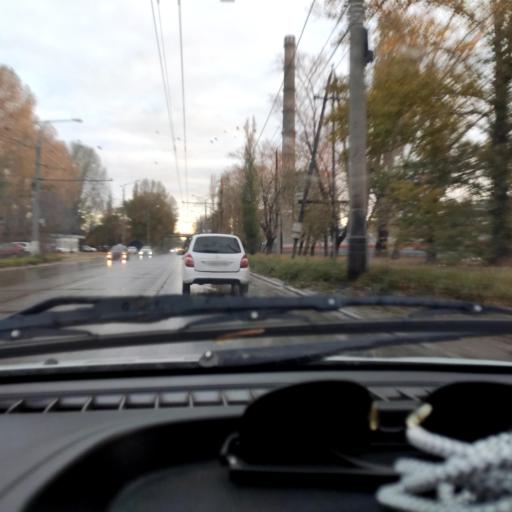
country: RU
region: Samara
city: Tol'yatti
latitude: 53.5471
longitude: 49.4468
